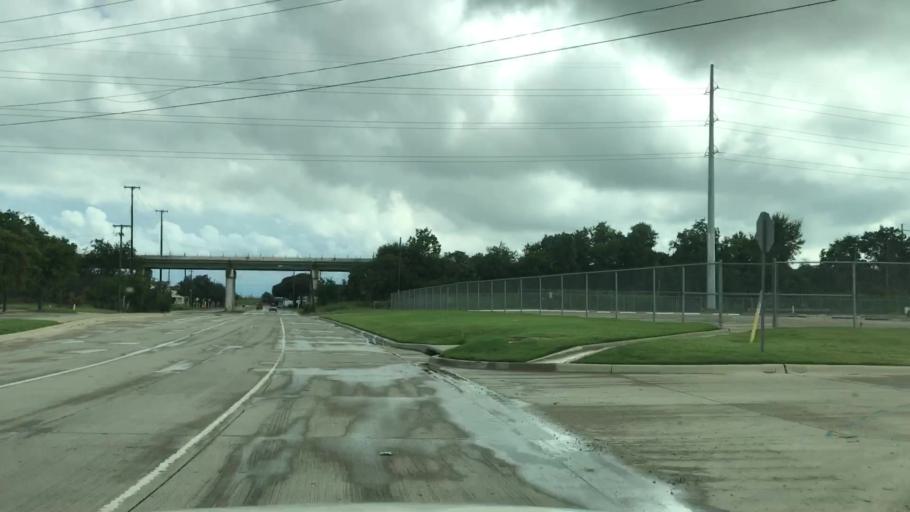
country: US
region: Texas
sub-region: Dallas County
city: Irving
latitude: 32.8155
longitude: -96.9002
